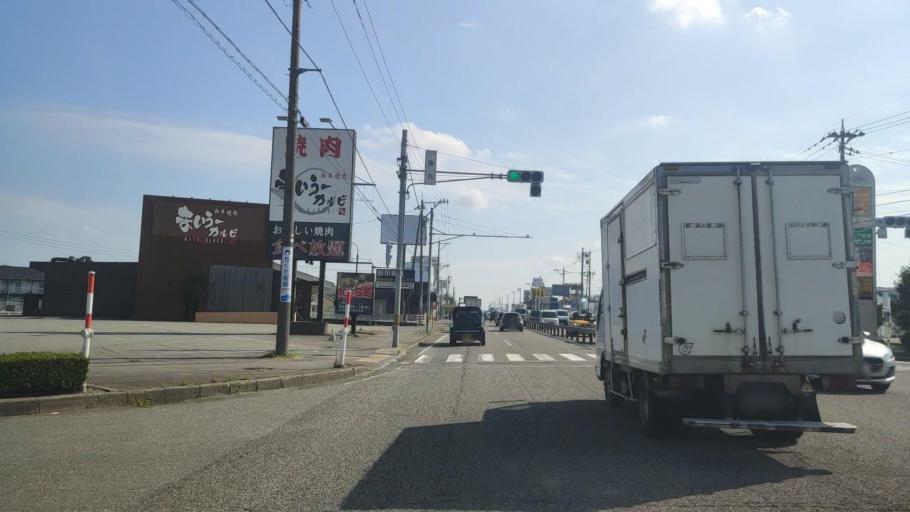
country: JP
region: Ishikawa
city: Matsuto
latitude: 36.5182
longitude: 136.5773
